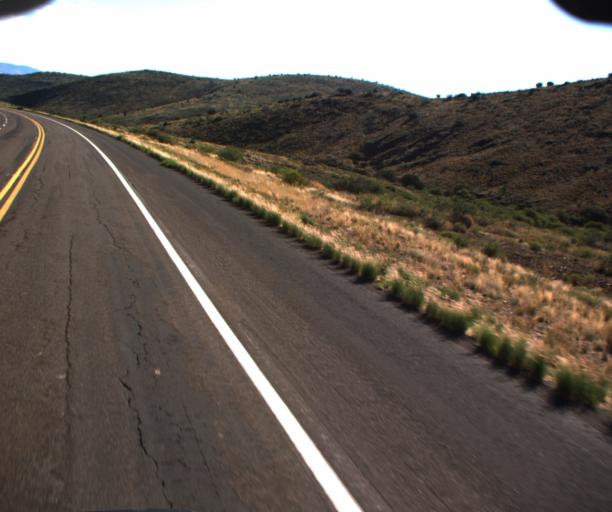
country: US
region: Arizona
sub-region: Greenlee County
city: Clifton
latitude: 32.8734
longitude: -109.2866
